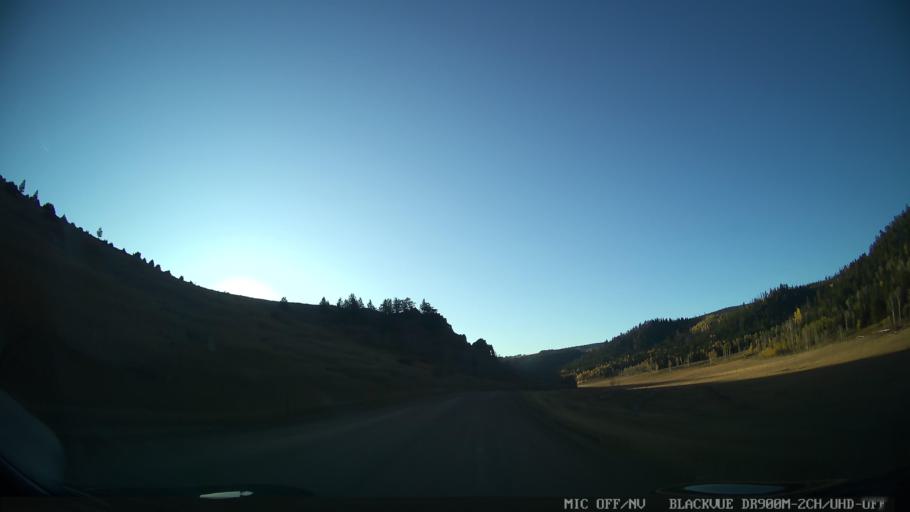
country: US
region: Colorado
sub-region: Grand County
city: Kremmling
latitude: 39.9905
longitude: -106.4457
